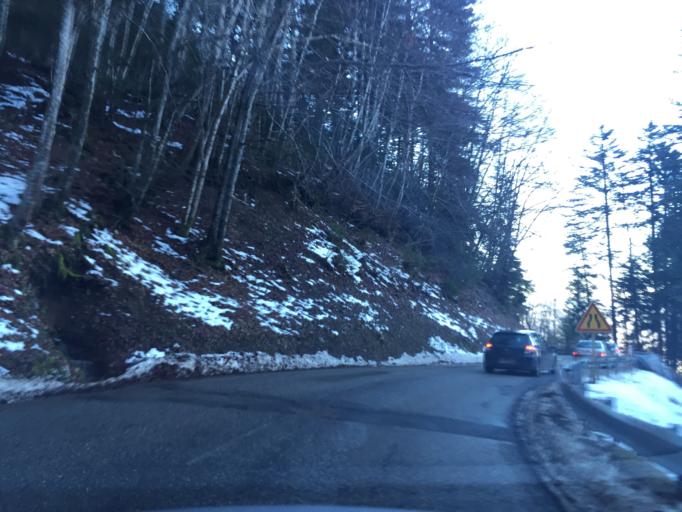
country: FR
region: Rhone-Alpes
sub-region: Departement de la Haute-Savoie
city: Cusy
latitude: 45.7017
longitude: 6.0025
